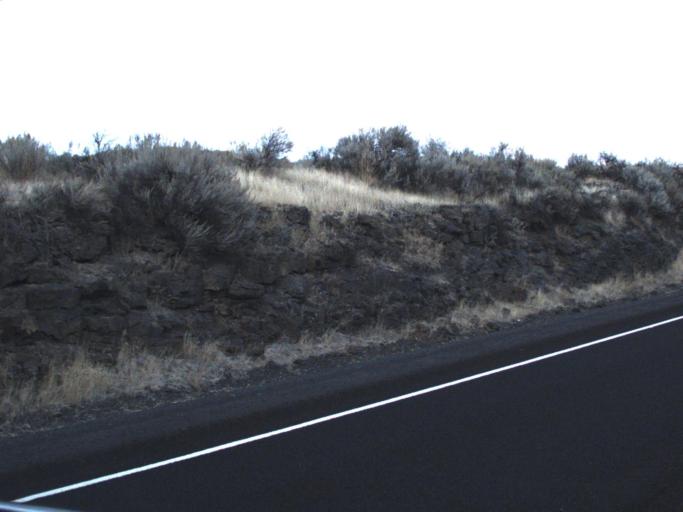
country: US
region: Washington
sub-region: Adams County
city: Ritzville
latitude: 47.3670
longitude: -118.4584
